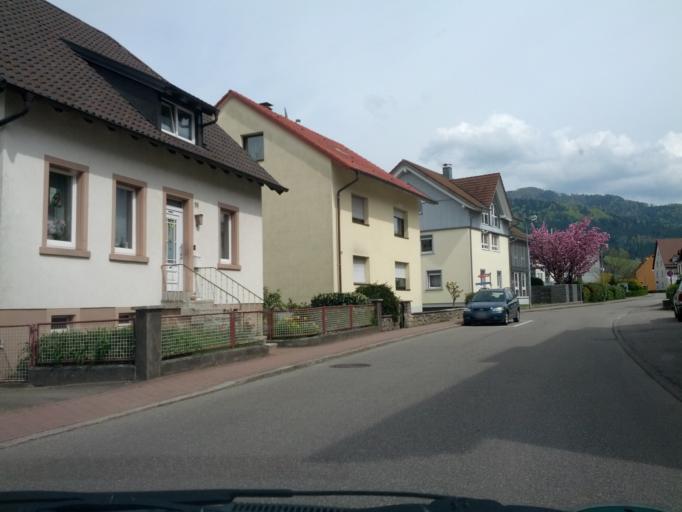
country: DE
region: Baden-Wuerttemberg
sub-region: Freiburg Region
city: Gutach im Breisgau
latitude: 48.1221
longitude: 8.0042
